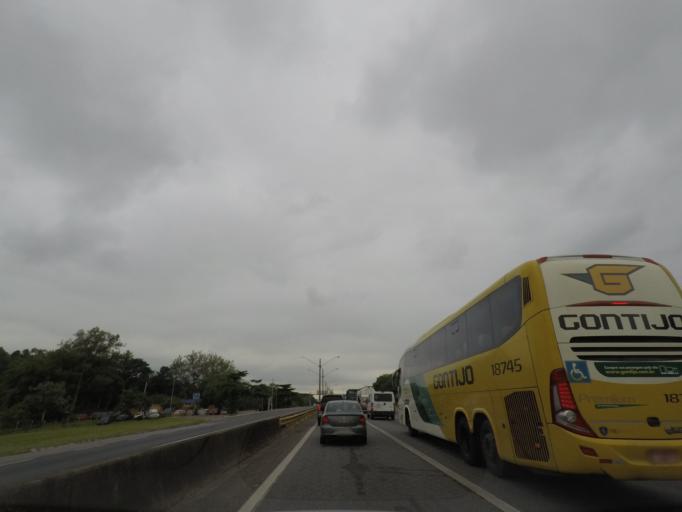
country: BR
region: Sao Paulo
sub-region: Aparecida
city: Aparecida
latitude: -22.8926
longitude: -45.2924
